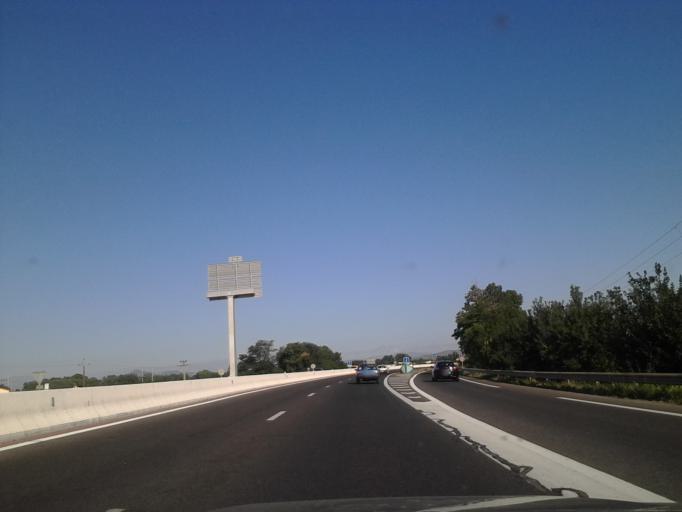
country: FR
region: Languedoc-Roussillon
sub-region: Departement des Pyrenees-Orientales
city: Perpignan
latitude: 42.7088
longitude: 2.8780
